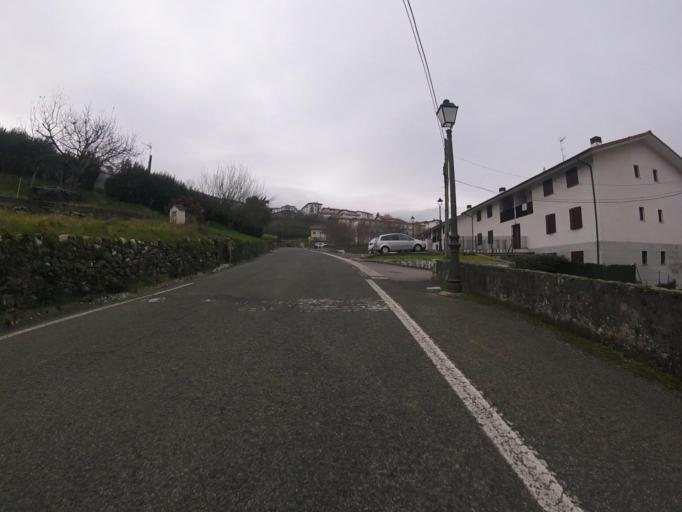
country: ES
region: Navarre
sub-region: Provincia de Navarra
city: Arantza
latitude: 43.1983
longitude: -1.7245
